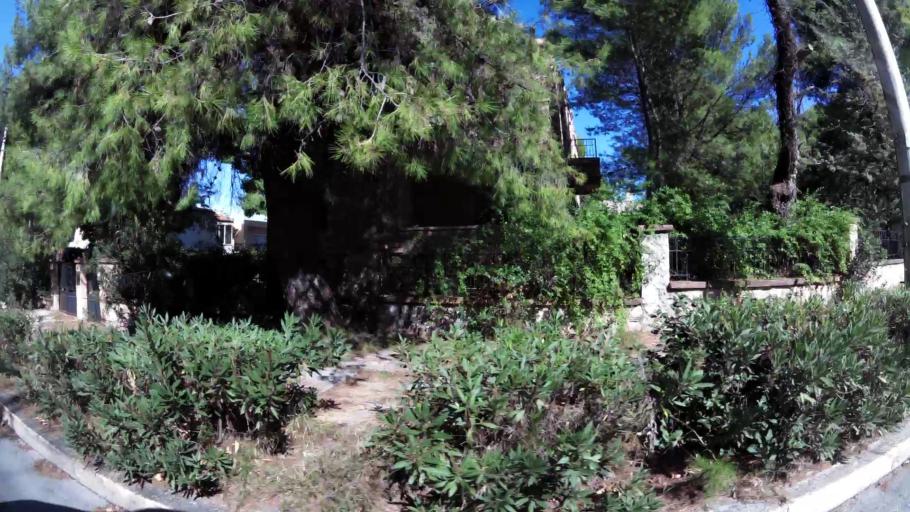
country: GR
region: Attica
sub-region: Nomarchia Athinas
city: Ekali
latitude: 38.1137
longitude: 23.8388
